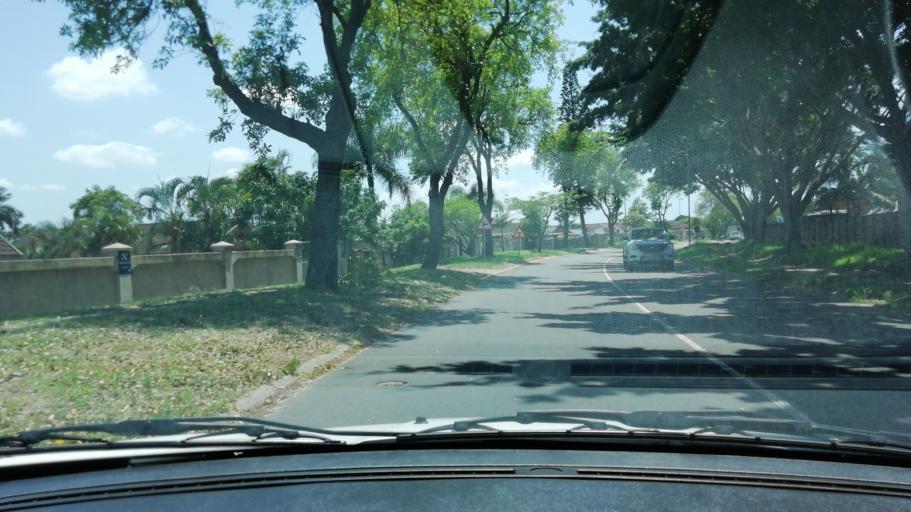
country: ZA
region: KwaZulu-Natal
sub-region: uThungulu District Municipality
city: Richards Bay
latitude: -28.7378
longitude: 32.0544
